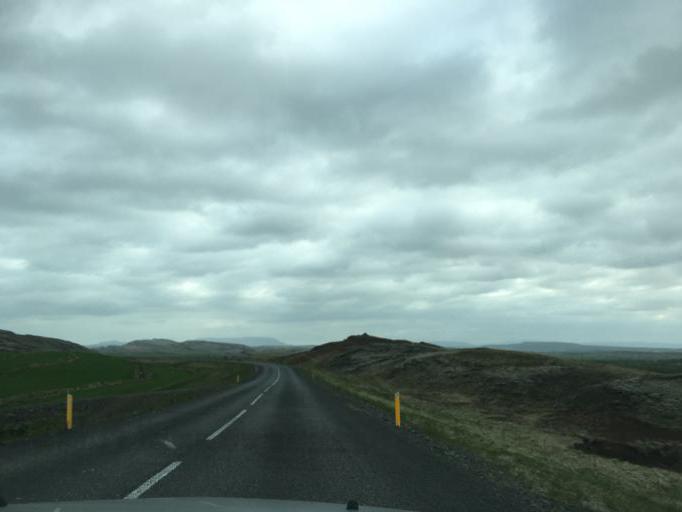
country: IS
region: South
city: Vestmannaeyjar
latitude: 64.2316
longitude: -20.2432
